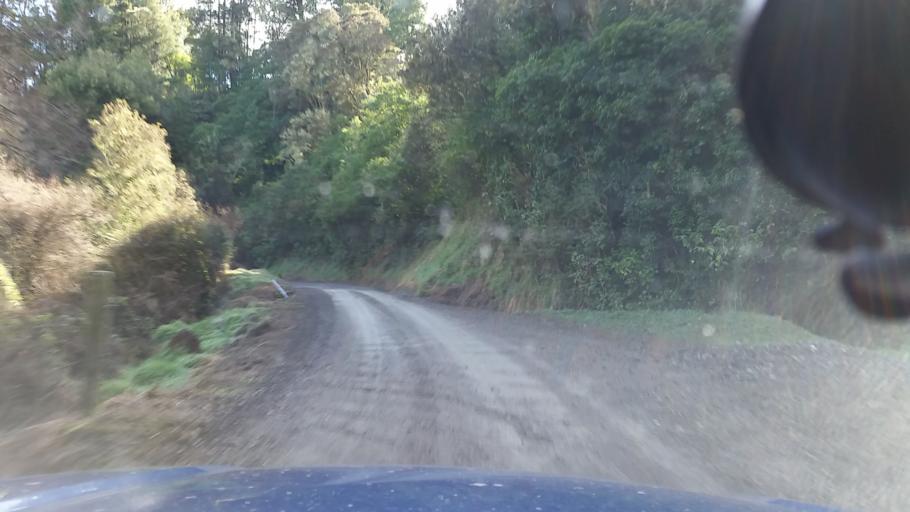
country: NZ
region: Taranaki
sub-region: New Plymouth District
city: Waitara
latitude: -39.0620
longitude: 174.7879
